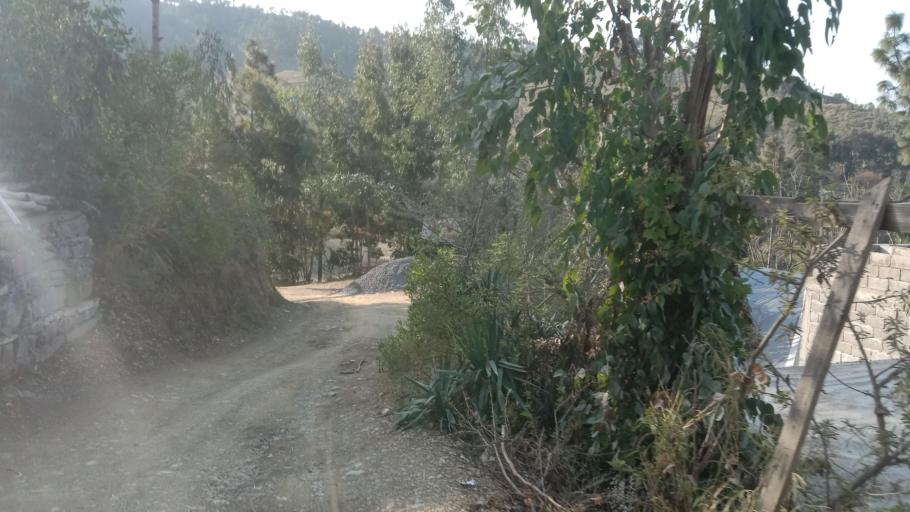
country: PK
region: Khyber Pakhtunkhwa
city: Abbottabad
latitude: 34.2050
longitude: 73.2062
